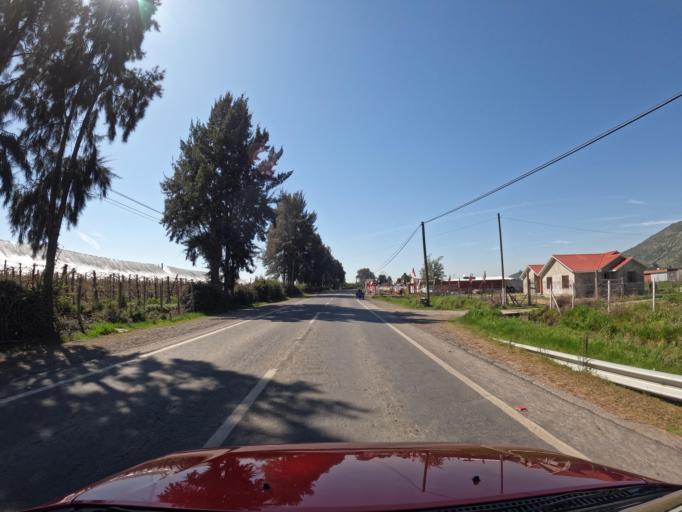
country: CL
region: Maule
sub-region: Provincia de Curico
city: Rauco
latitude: -35.0084
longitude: -71.4113
